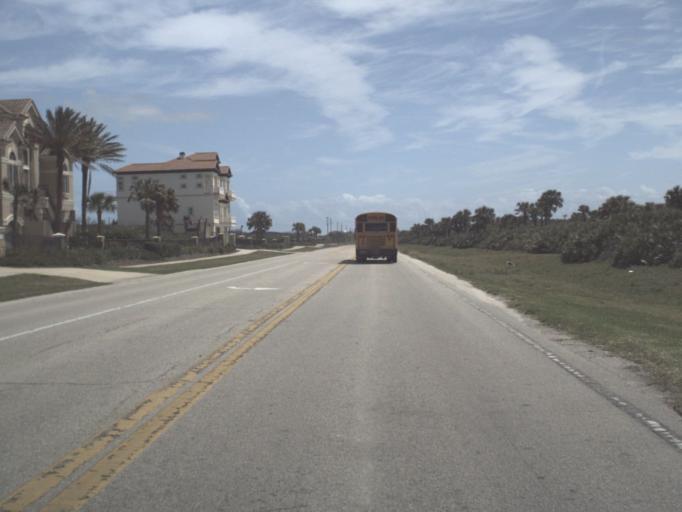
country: US
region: Florida
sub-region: Flagler County
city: Palm Coast
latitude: 29.5556
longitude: -81.1649
